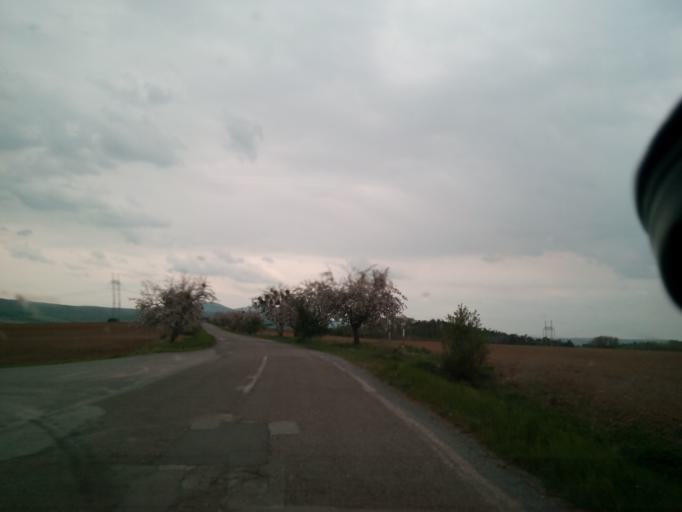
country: SK
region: Kosicky
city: Secovce
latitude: 48.7616
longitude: 21.4655
